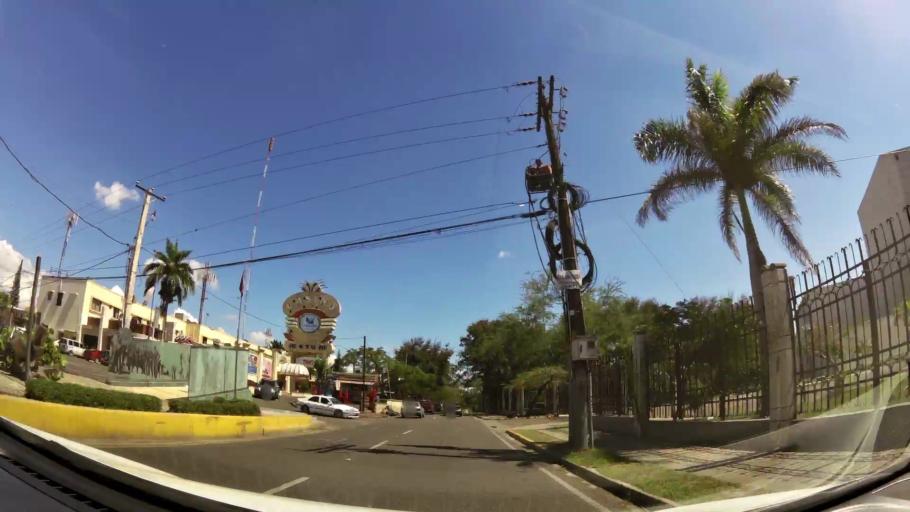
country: DO
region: Santiago
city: Santiago de los Caballeros
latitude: 19.4520
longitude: -70.6919
